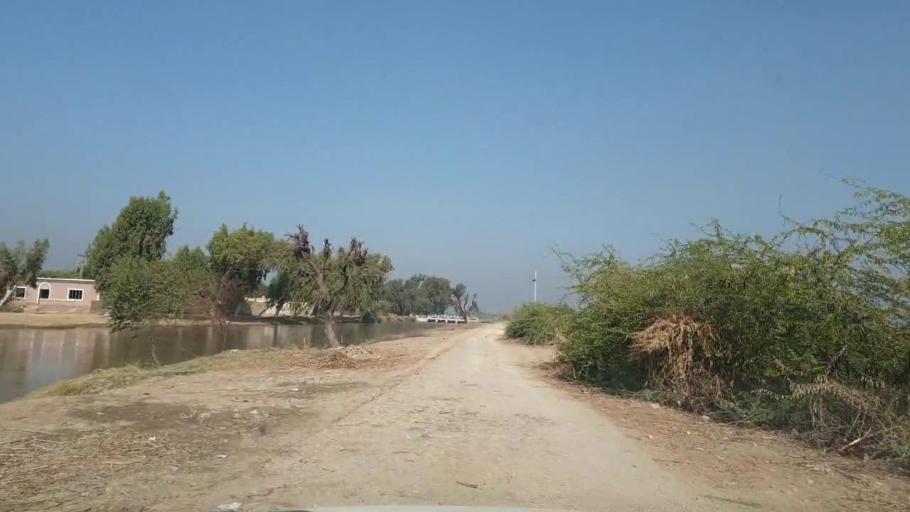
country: PK
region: Sindh
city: Mirpur Khas
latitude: 25.5055
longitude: 69.1222
